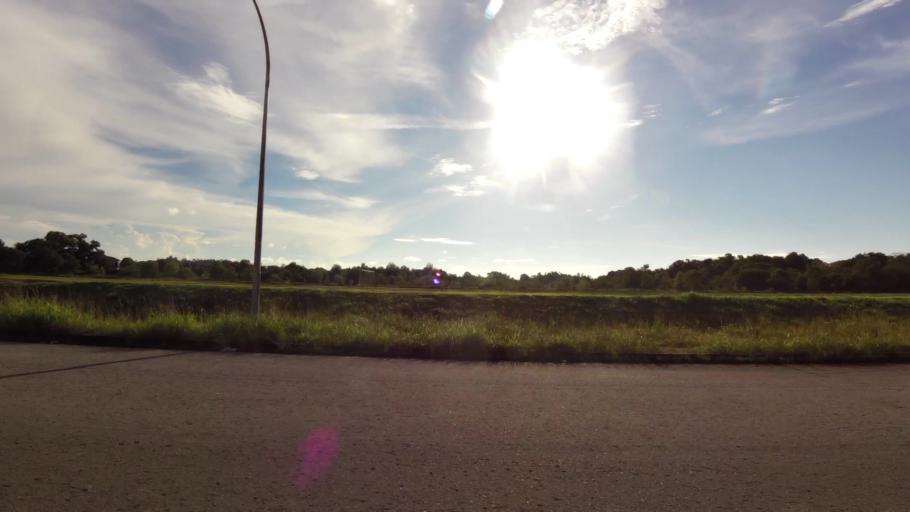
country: BN
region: Brunei and Muara
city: Bandar Seri Begawan
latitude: 4.9820
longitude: 114.9756
